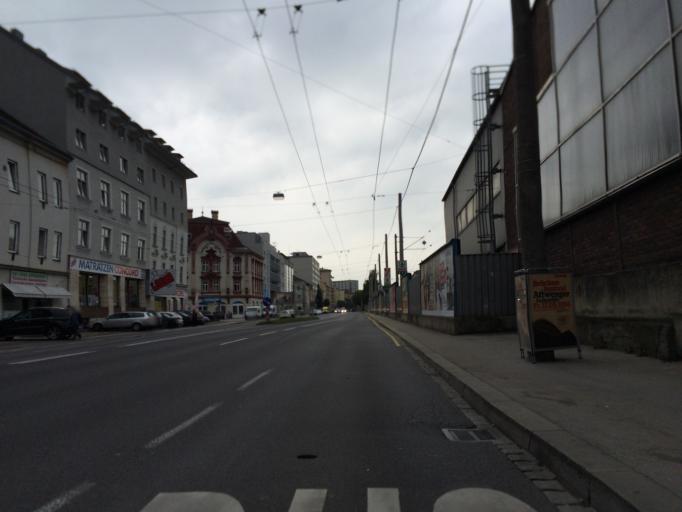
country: AT
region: Upper Austria
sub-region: Linz Stadt
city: Linz
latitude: 48.2897
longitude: 14.2964
